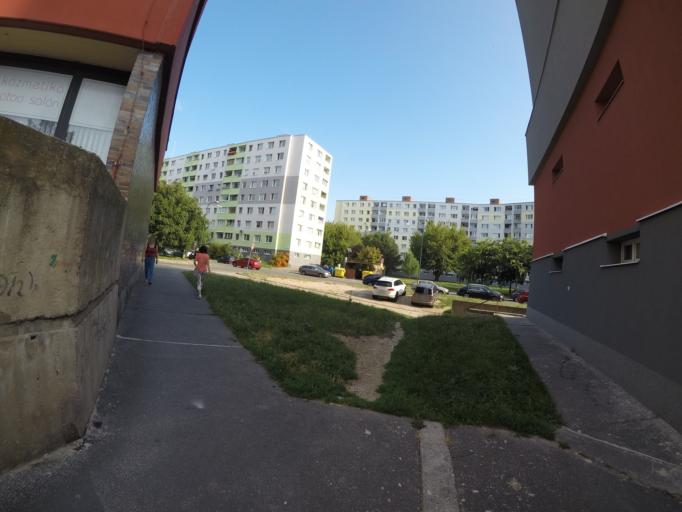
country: SK
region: Bratislavsky
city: Bratislava
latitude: 48.1181
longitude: 17.1041
